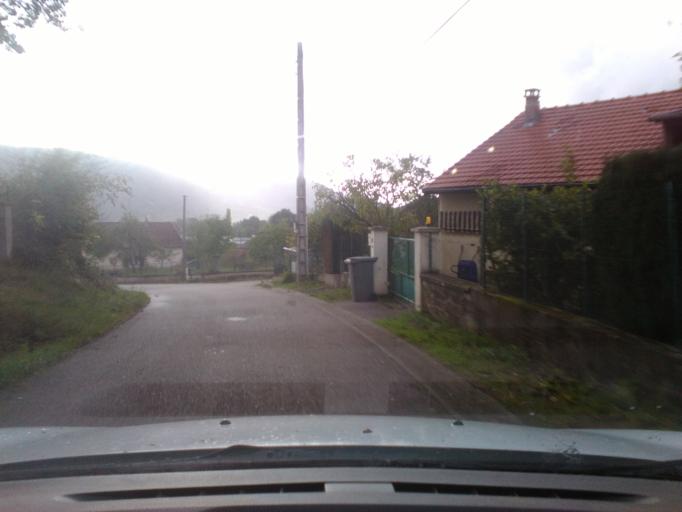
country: FR
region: Lorraine
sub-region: Departement des Vosges
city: Saint-Die-des-Vosges
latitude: 48.3118
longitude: 6.9356
